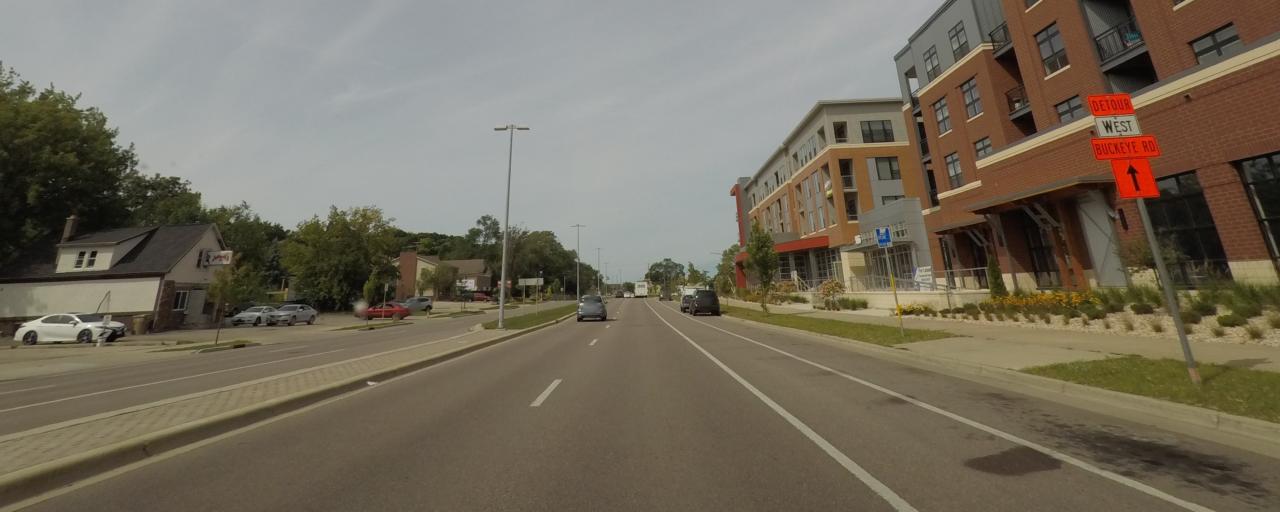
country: US
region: Wisconsin
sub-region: Dane County
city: Monona
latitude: 43.0840
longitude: -89.3166
